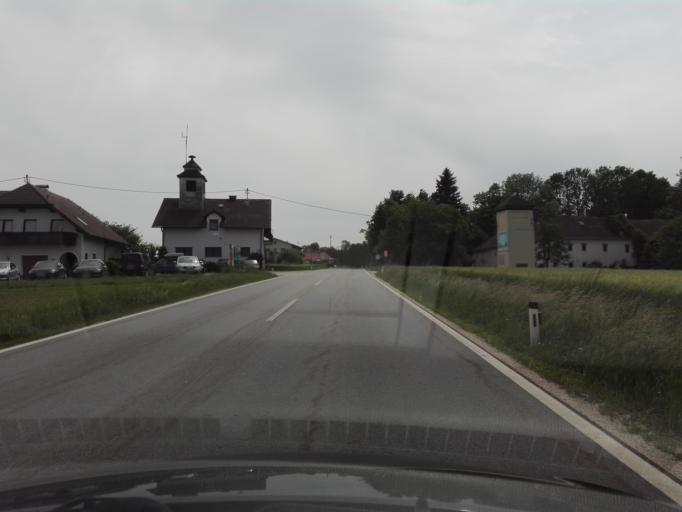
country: AT
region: Upper Austria
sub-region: Politischer Bezirk Kirchdorf an der Krems
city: Kremsmunster
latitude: 48.0624
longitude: 14.1020
